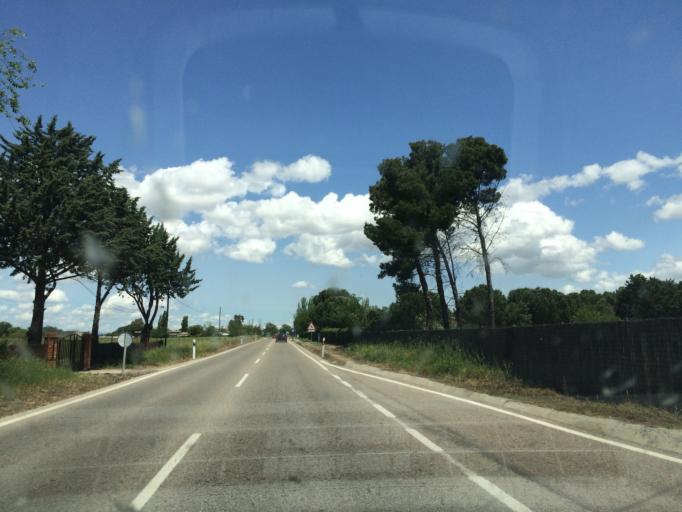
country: ES
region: Madrid
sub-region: Provincia de Madrid
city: Fuente el Saz
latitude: 40.6431
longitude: -3.5070
